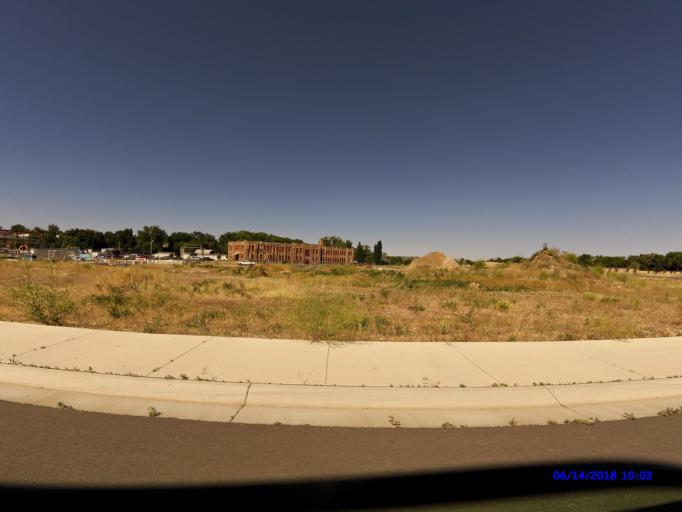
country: US
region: Utah
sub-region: Weber County
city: Ogden
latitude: 41.2261
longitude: -111.9901
